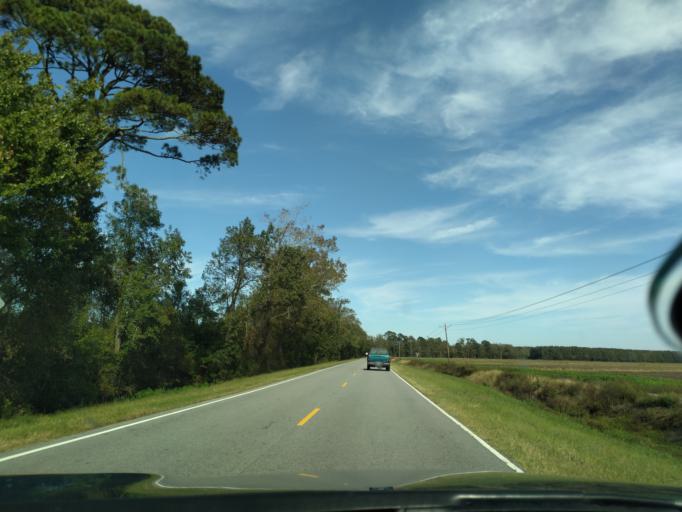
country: US
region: North Carolina
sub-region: Beaufort County
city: Belhaven
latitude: 35.6235
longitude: -76.6336
